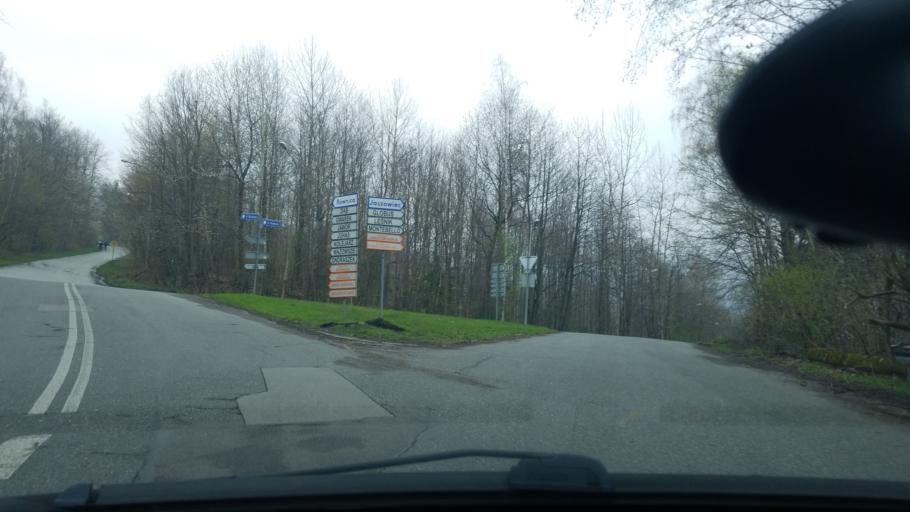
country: PL
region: Silesian Voivodeship
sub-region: Powiat cieszynski
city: Ustron
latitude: 49.7023
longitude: 18.8353
